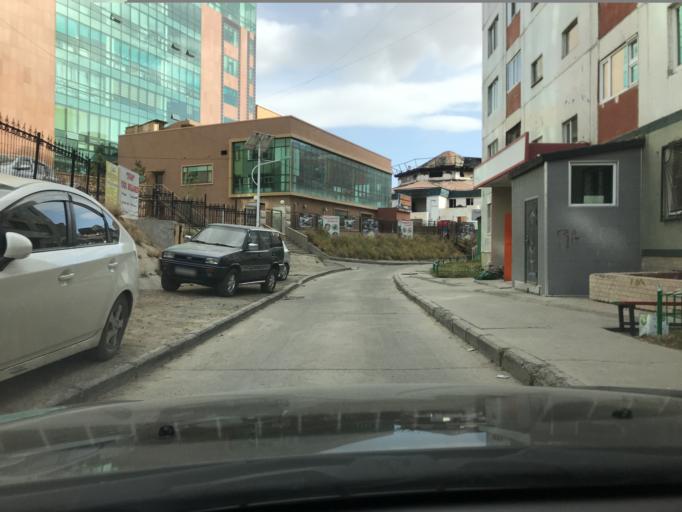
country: MN
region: Ulaanbaatar
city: Ulaanbaatar
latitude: 47.9183
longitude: 106.9407
